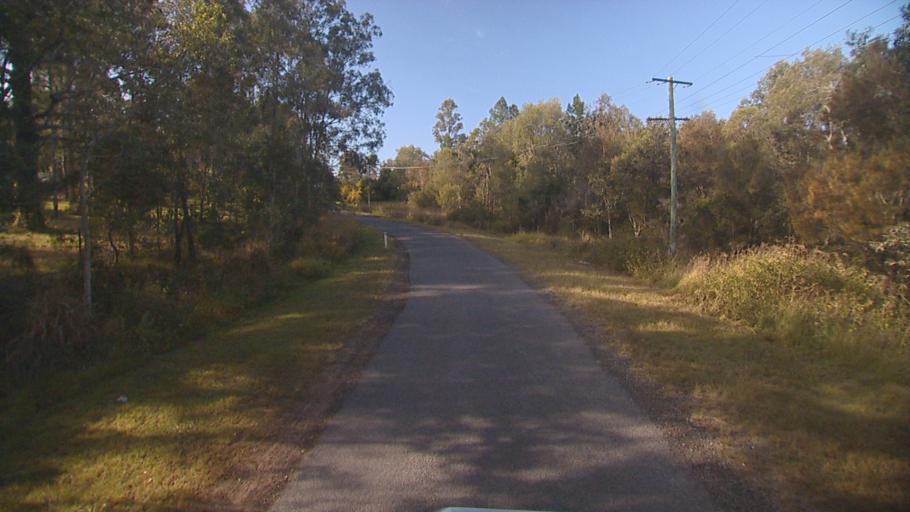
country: AU
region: Queensland
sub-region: Logan
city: Park Ridge South
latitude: -27.7473
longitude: 153.0385
